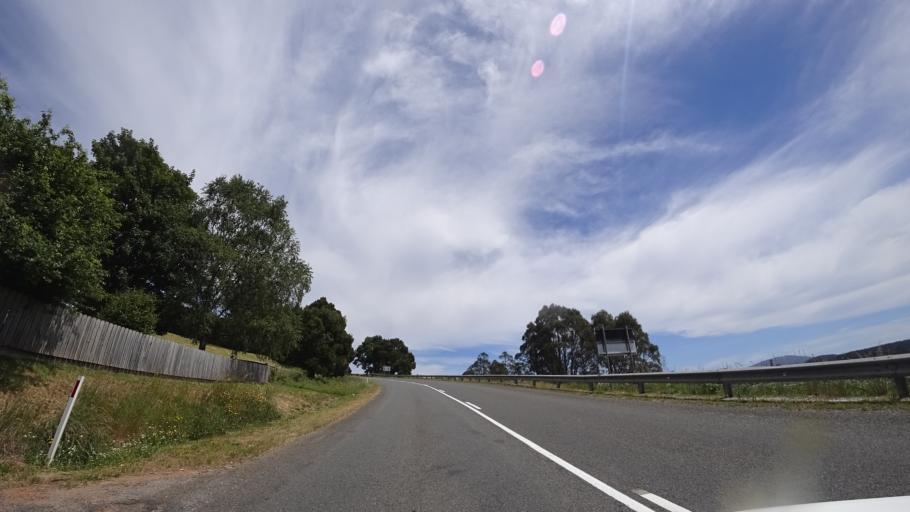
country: AU
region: Tasmania
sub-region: Dorset
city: Scottsdale
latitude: -41.1691
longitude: 147.7360
